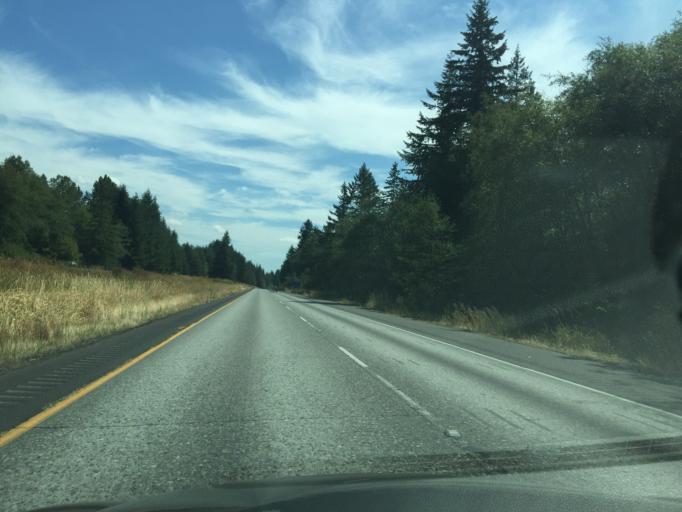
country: US
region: Washington
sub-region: Whatcom County
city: Sudden Valley
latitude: 48.5992
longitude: -122.3447
